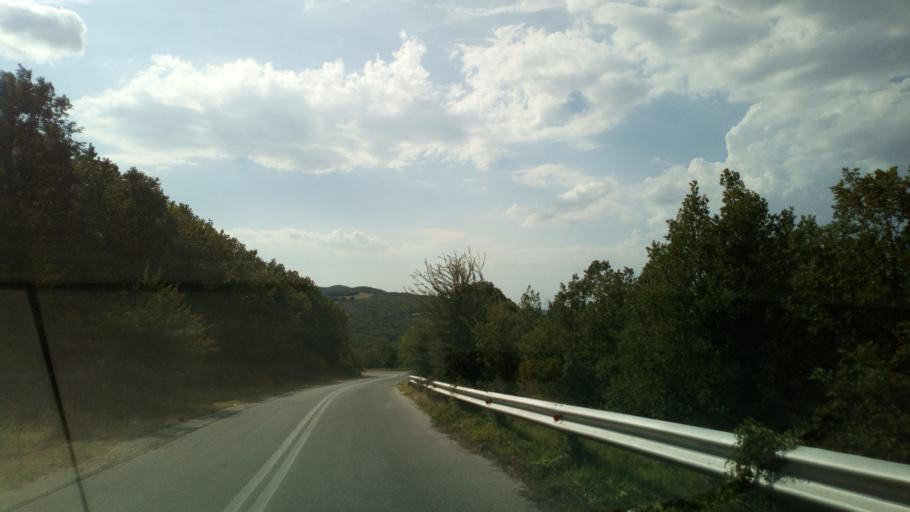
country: GR
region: Central Macedonia
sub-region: Nomos Chalkidikis
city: Polygyros
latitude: 40.4887
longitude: 23.3995
